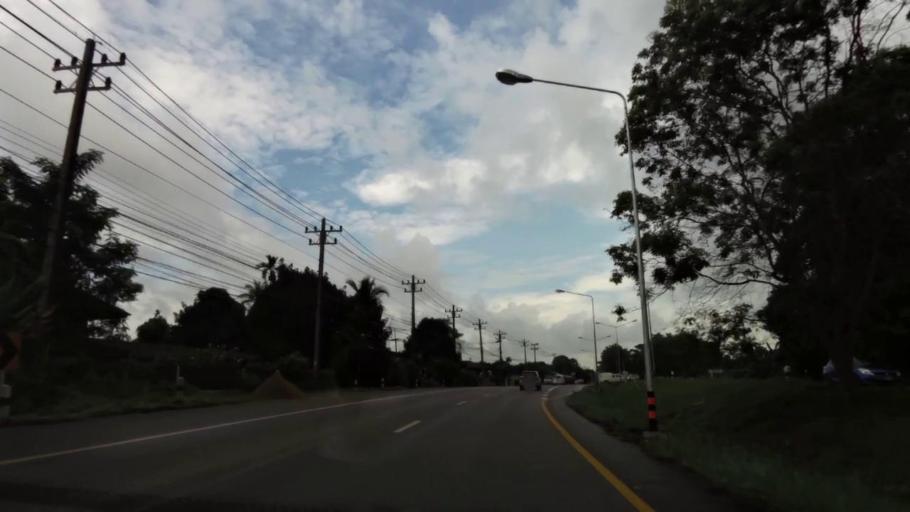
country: TH
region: Chanthaburi
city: Khlung
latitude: 12.4839
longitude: 102.1795
